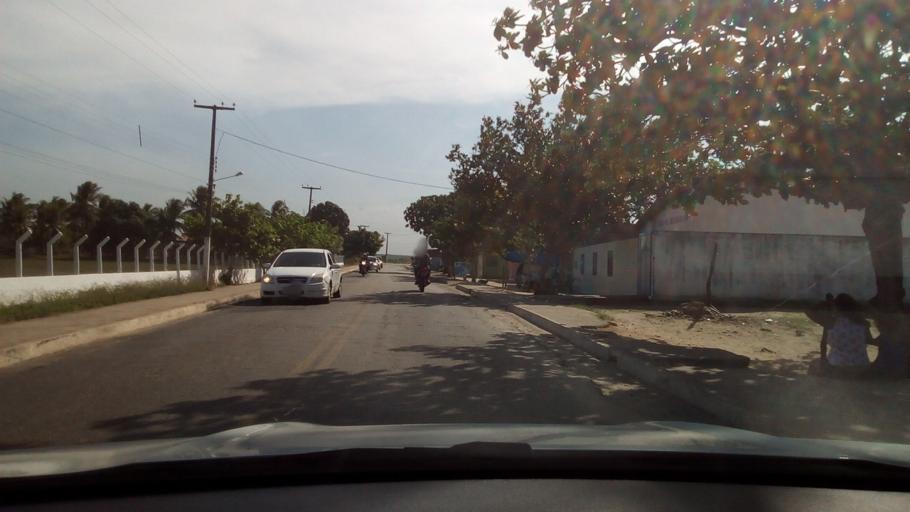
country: BR
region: Rio Grande do Norte
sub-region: Goianinha
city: Goianinha
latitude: -6.2420
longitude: -35.1793
